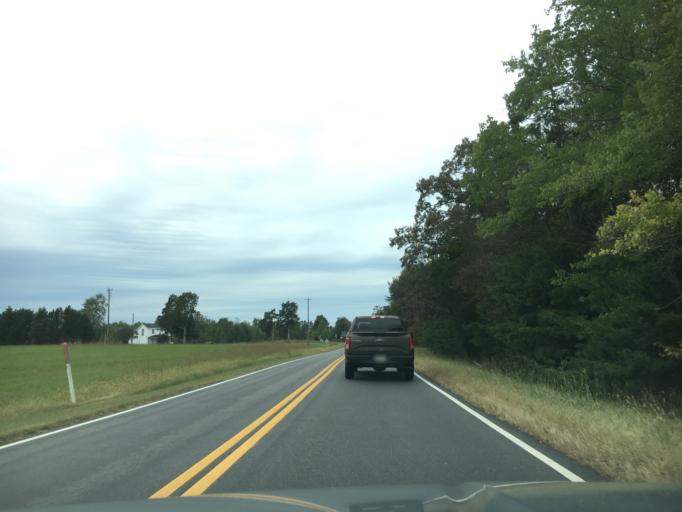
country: US
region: Virginia
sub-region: Louisa County
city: Louisa
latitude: 37.8422
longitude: -77.9958
